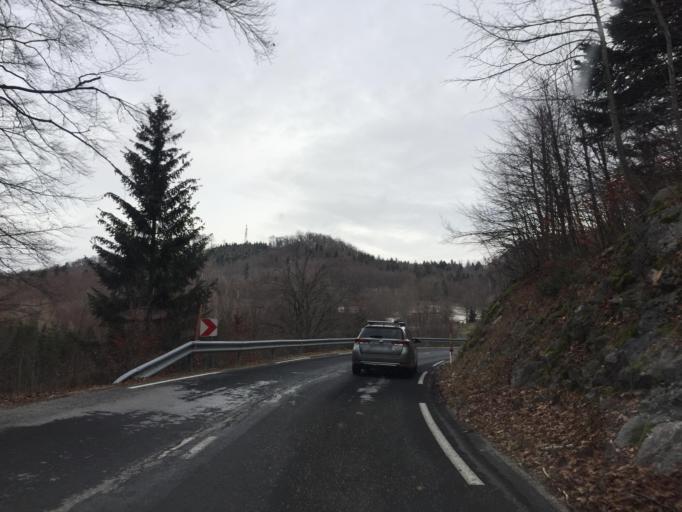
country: SI
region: Nova Gorica
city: Sempas
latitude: 46.0086
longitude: 13.7827
